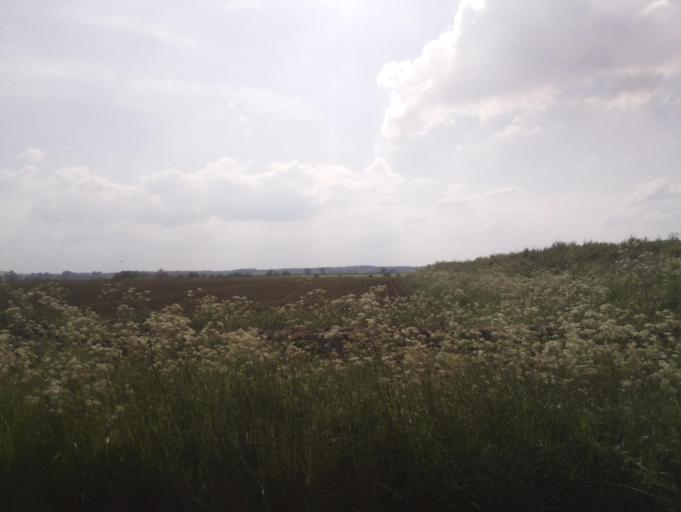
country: GB
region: England
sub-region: Wiltshire
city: Luckington
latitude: 51.5857
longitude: -2.2226
